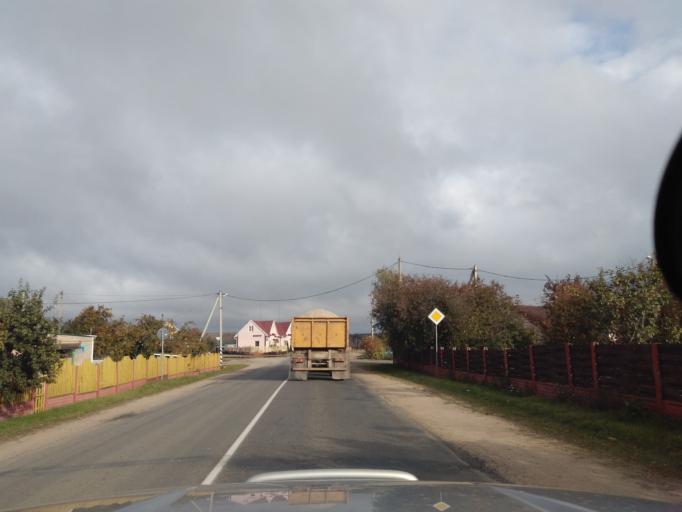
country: BY
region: Minsk
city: Kapyl'
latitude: 53.1516
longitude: 27.0744
